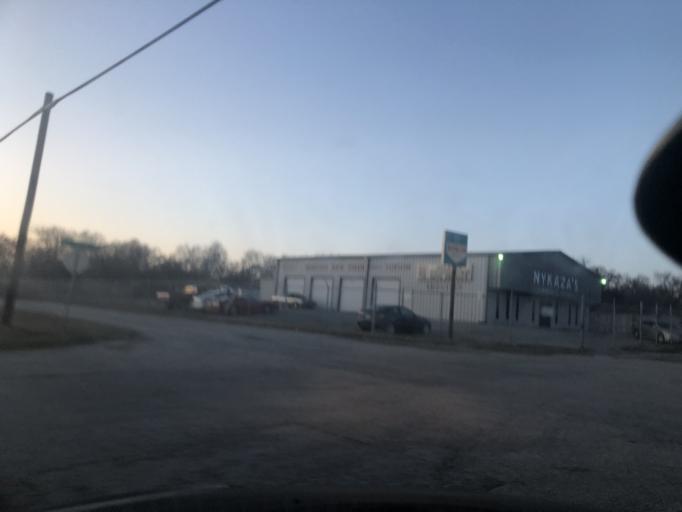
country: US
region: Texas
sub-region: Tarrant County
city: White Settlement
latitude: 32.7249
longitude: -97.4918
